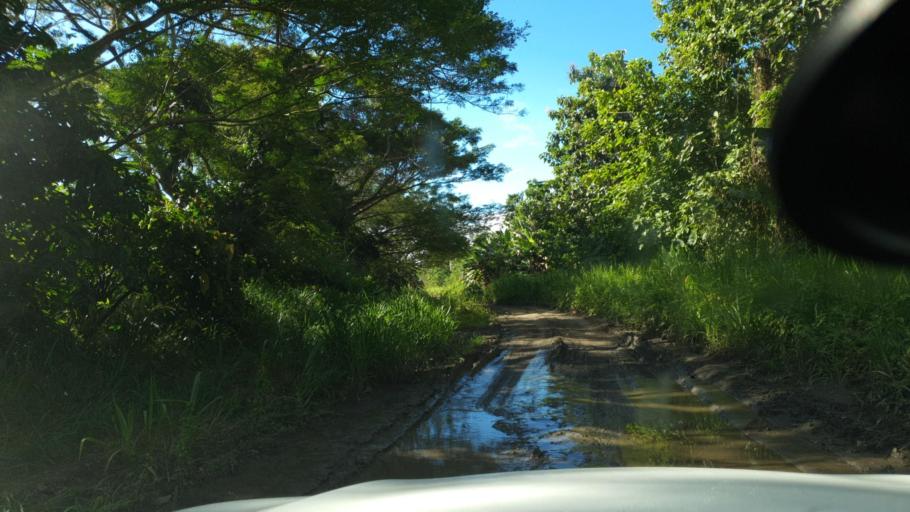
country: SB
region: Guadalcanal
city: Honiara
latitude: -9.4437
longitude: 160.1840
